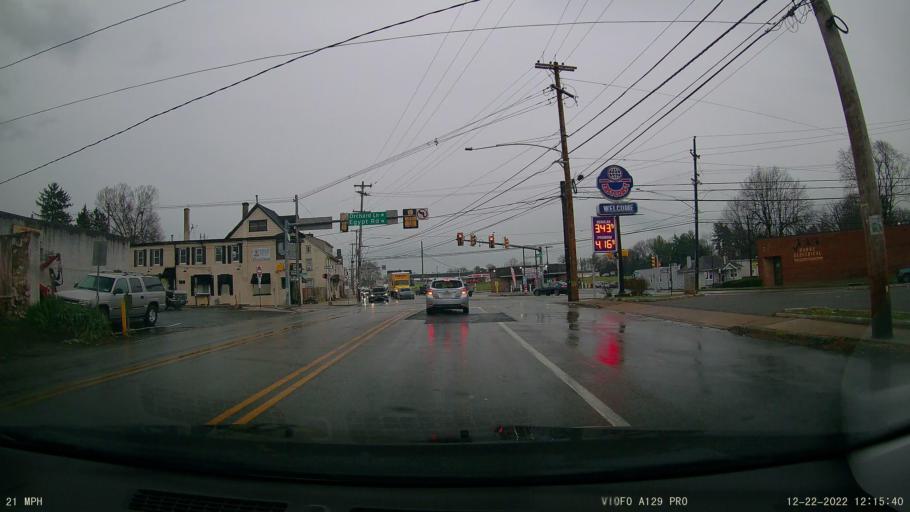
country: US
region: Pennsylvania
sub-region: Montgomery County
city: West Norriton
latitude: 40.1329
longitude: -75.3787
